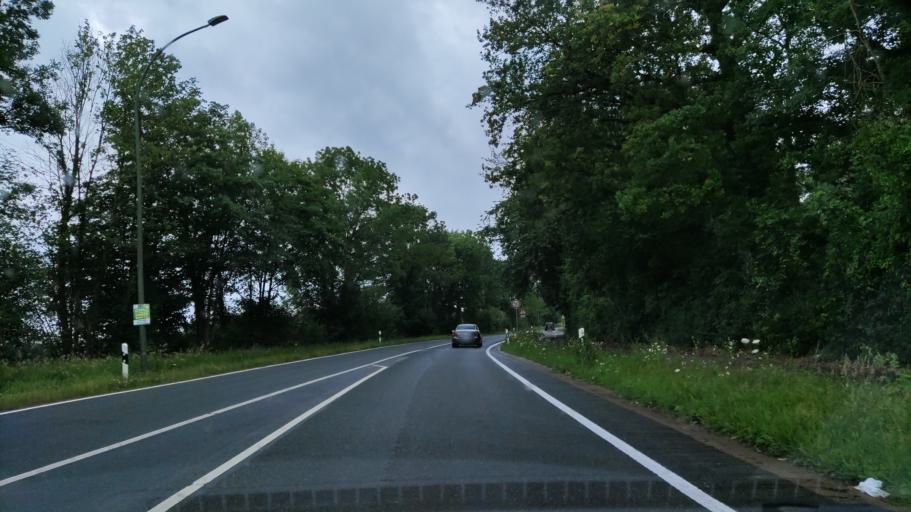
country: DE
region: North Rhine-Westphalia
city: Ahlen
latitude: 51.7355
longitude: 7.8801
